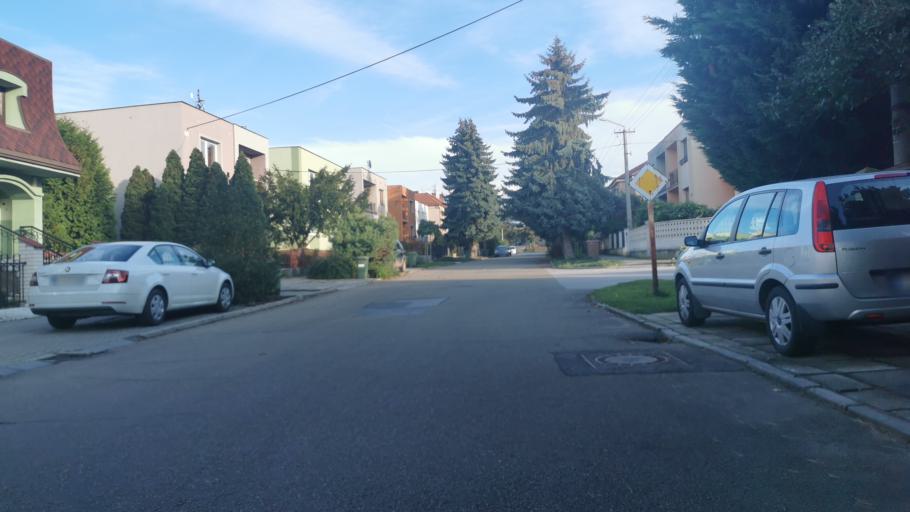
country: SK
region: Trnavsky
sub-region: Okres Skalica
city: Skalica
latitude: 48.8417
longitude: 17.2381
